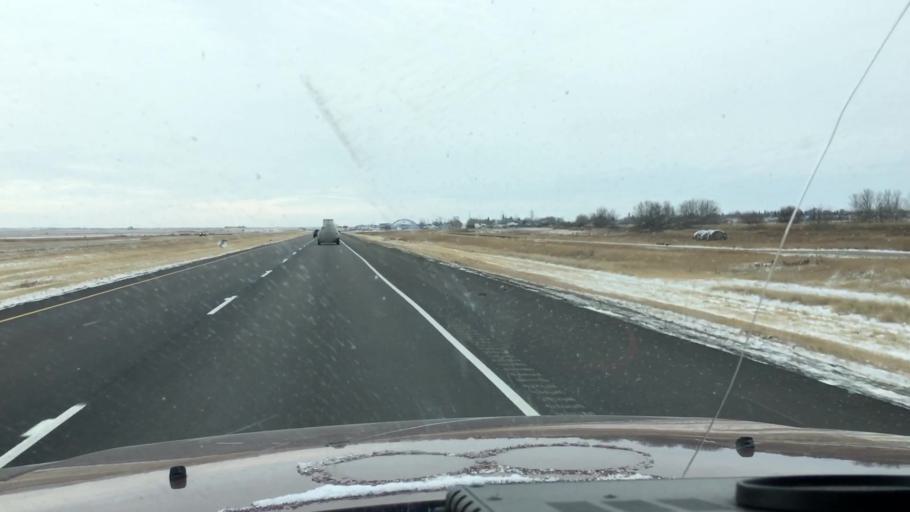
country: CA
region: Saskatchewan
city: Saskatoon
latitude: 51.8238
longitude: -106.5003
